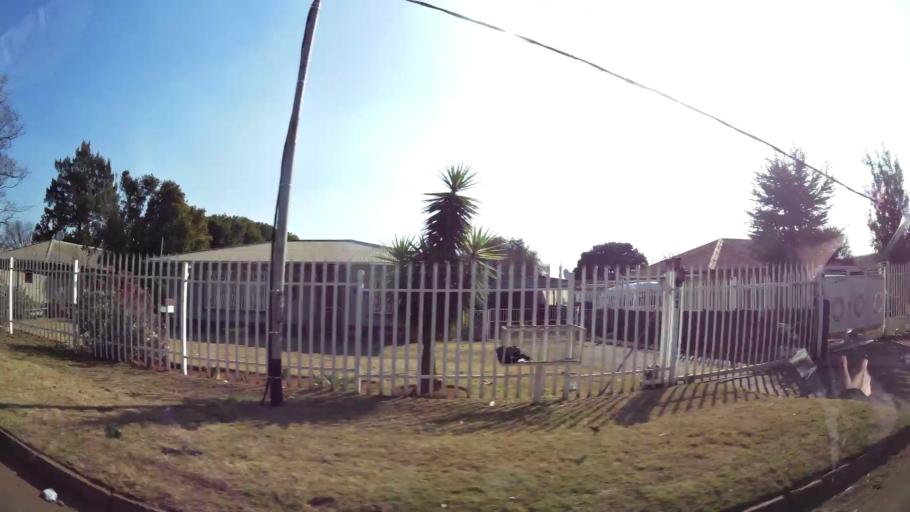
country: ZA
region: Gauteng
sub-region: West Rand District Municipality
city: Randfontein
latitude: -26.1845
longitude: 27.6940
